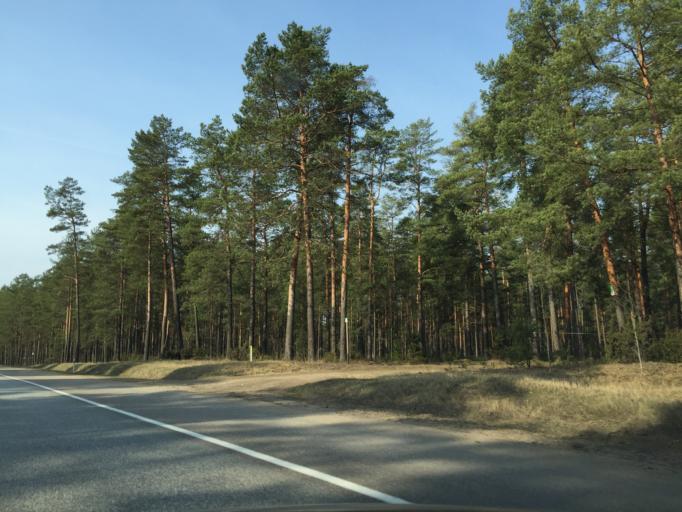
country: LV
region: Incukalns
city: Vangazi
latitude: 57.0771
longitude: 24.5107
